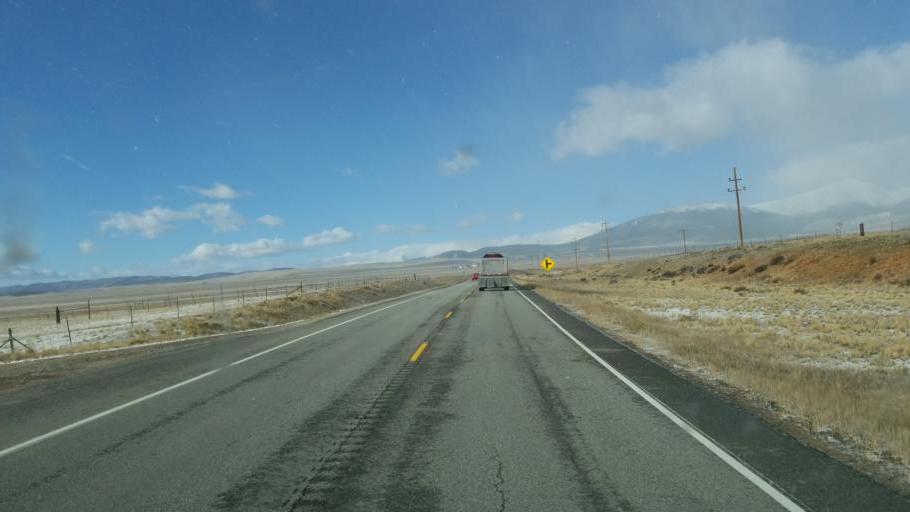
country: US
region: Colorado
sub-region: Park County
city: Fairplay
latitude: 39.3562
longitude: -105.8207
